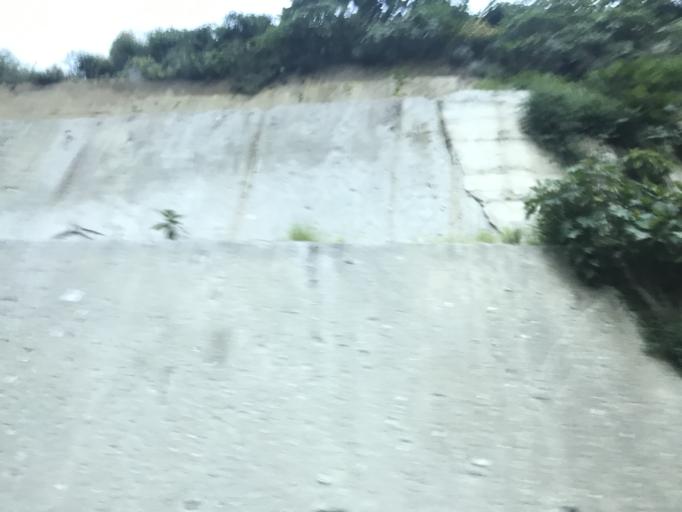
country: GT
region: Chimaltenango
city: El Tejar
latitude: 14.6386
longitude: -90.7904
